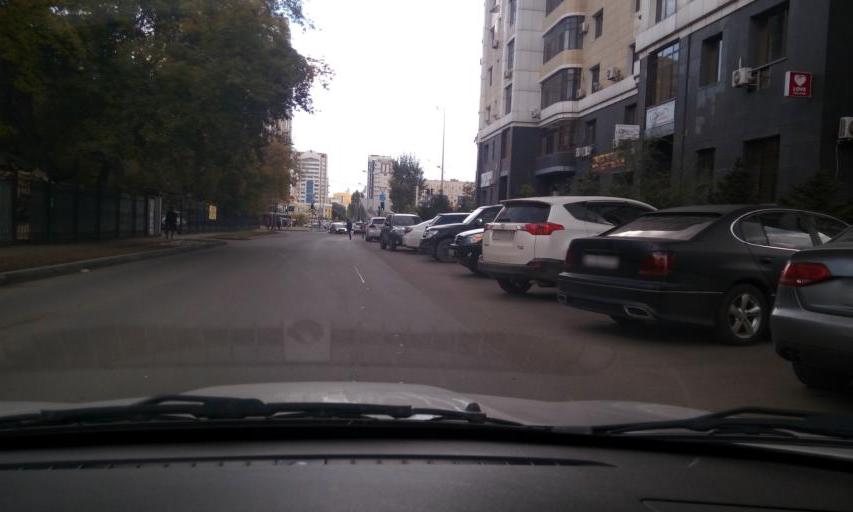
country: KZ
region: Astana Qalasy
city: Astana
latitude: 51.1670
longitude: 71.4312
